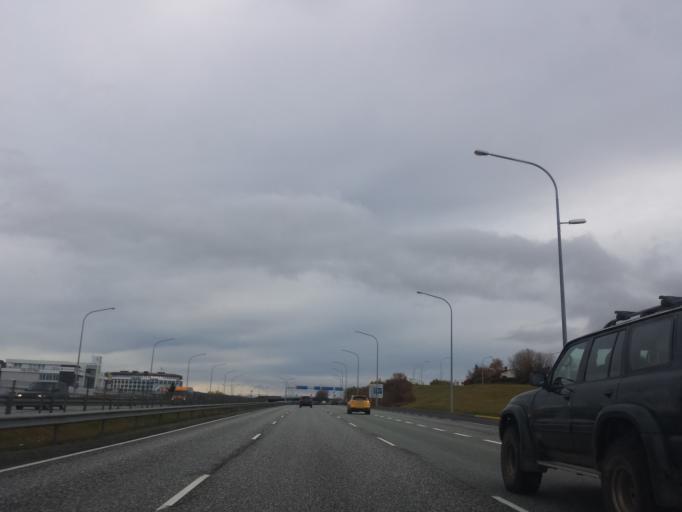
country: IS
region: Capital Region
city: Reykjavik
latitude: 64.1239
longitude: -21.8217
